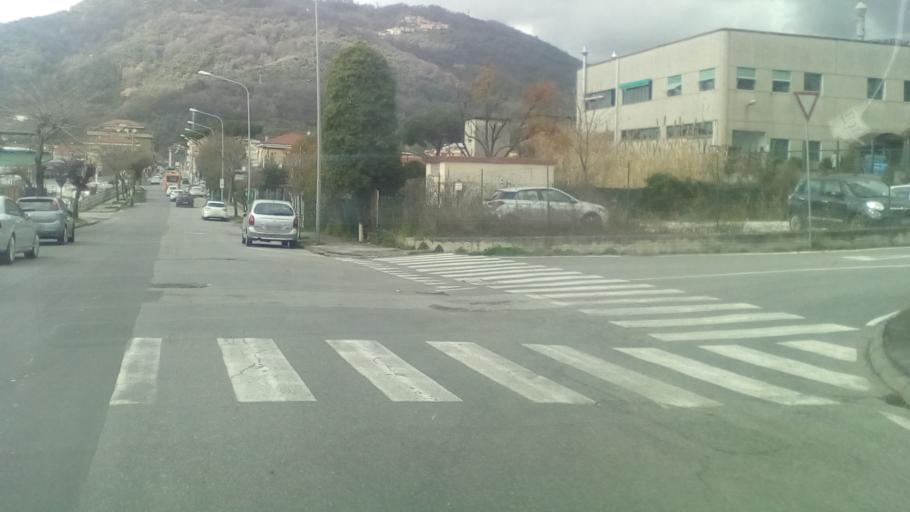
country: IT
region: Tuscany
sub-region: Provincia di Massa-Carrara
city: Carrara
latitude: 44.0617
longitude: 10.0815
